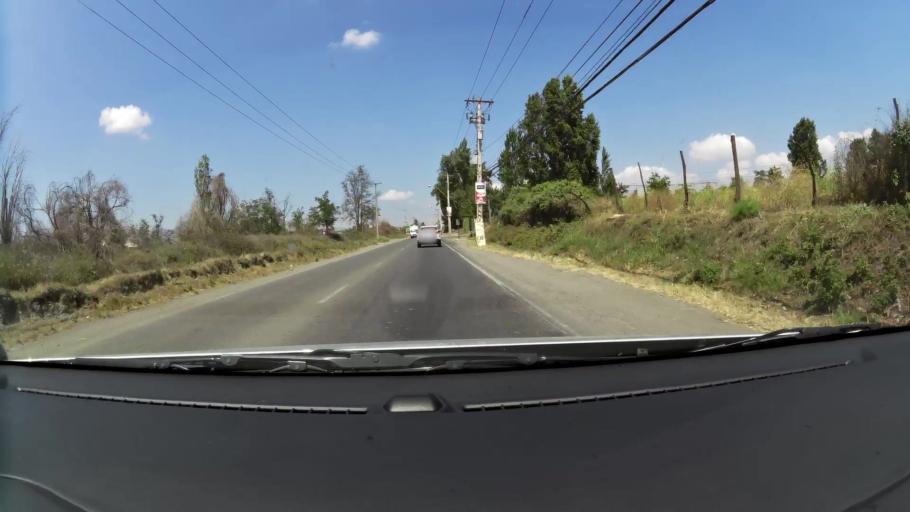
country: CL
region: Santiago Metropolitan
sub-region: Provincia de Maipo
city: San Bernardo
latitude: -33.5363
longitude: -70.7367
